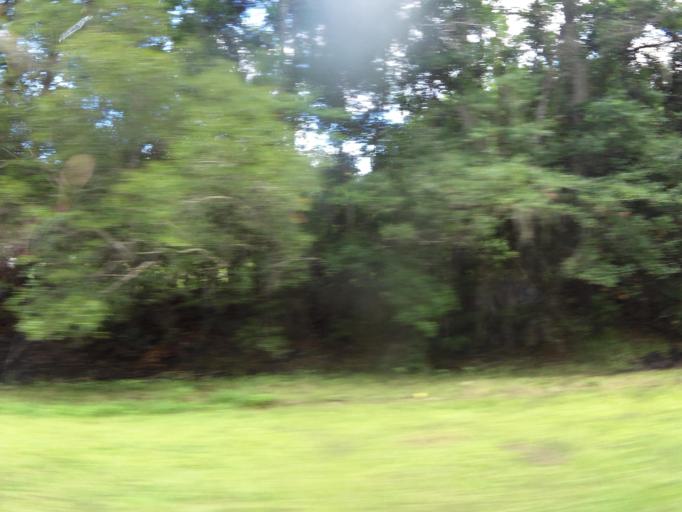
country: US
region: Georgia
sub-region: Camden County
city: St. Marys
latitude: 30.7346
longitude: -81.5501
